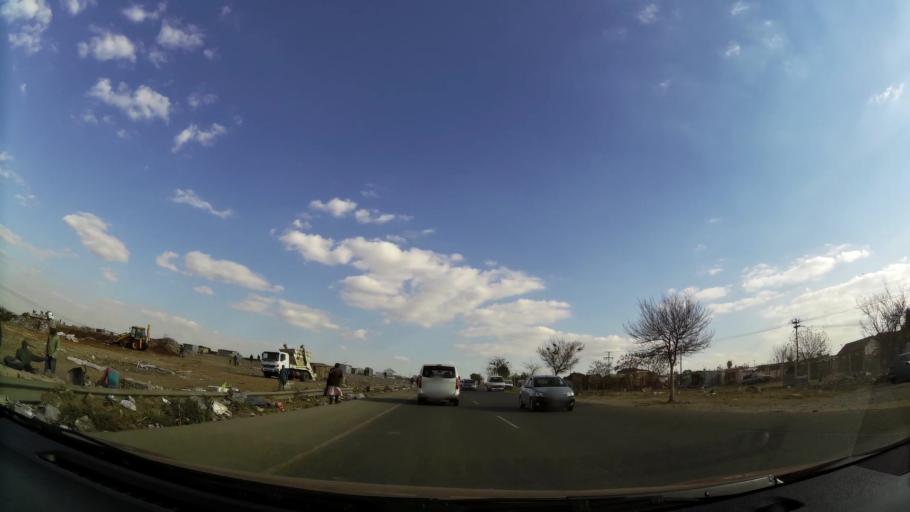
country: ZA
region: Gauteng
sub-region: Ekurhuleni Metropolitan Municipality
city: Tembisa
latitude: -25.9943
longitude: 28.1885
